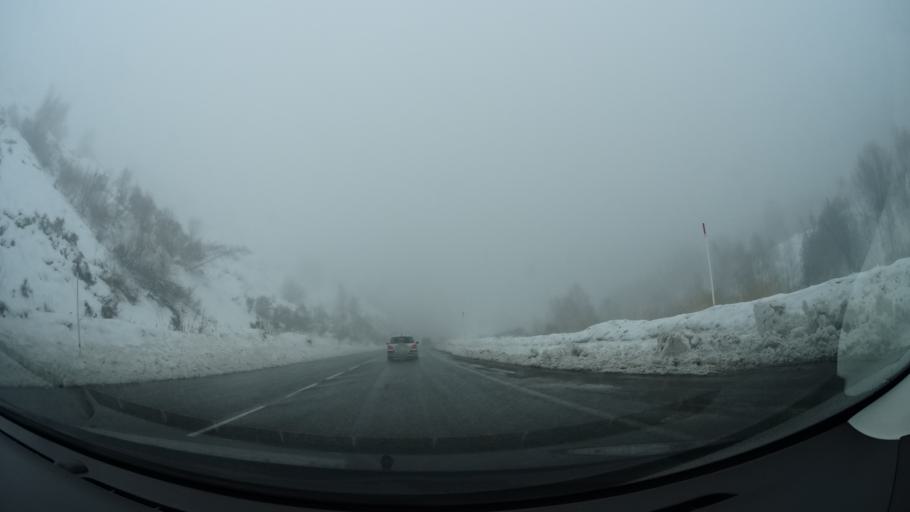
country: AD
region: Encamp
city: Pas de la Casa
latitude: 42.5766
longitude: 1.7891
